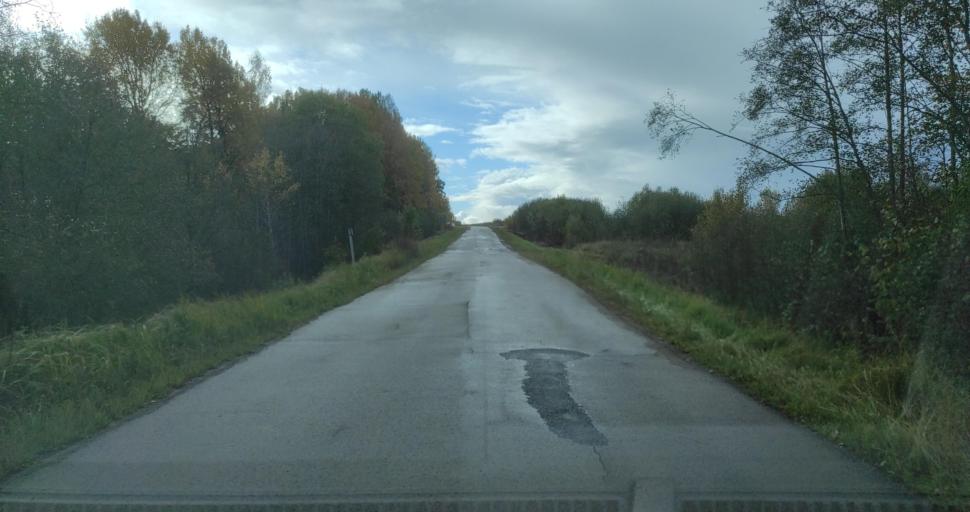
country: LV
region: Vainode
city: Vainode
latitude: 56.5628
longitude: 21.9068
